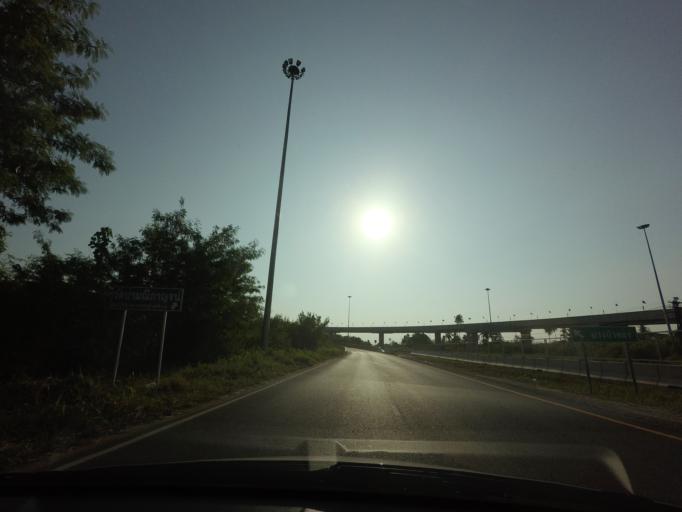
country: TH
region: Bangkok
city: Taling Chan
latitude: 13.7994
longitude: 100.4089
